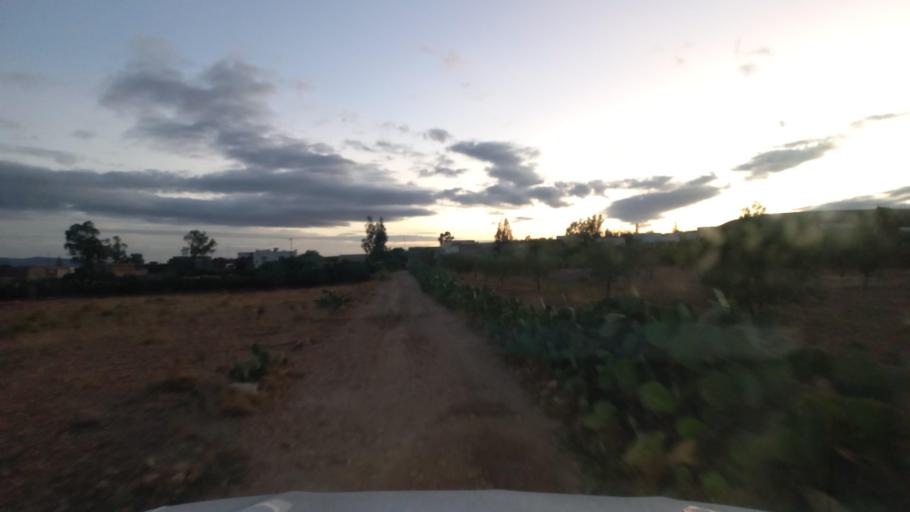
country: TN
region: Al Qasrayn
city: Kasserine
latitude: 35.2590
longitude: 8.9404
